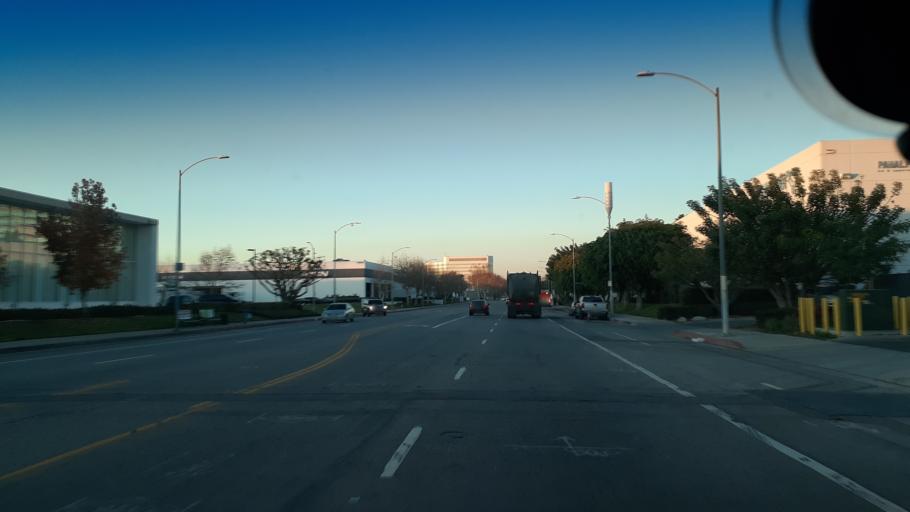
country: US
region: California
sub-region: Los Angeles County
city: Carson
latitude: 33.8490
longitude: -118.2905
